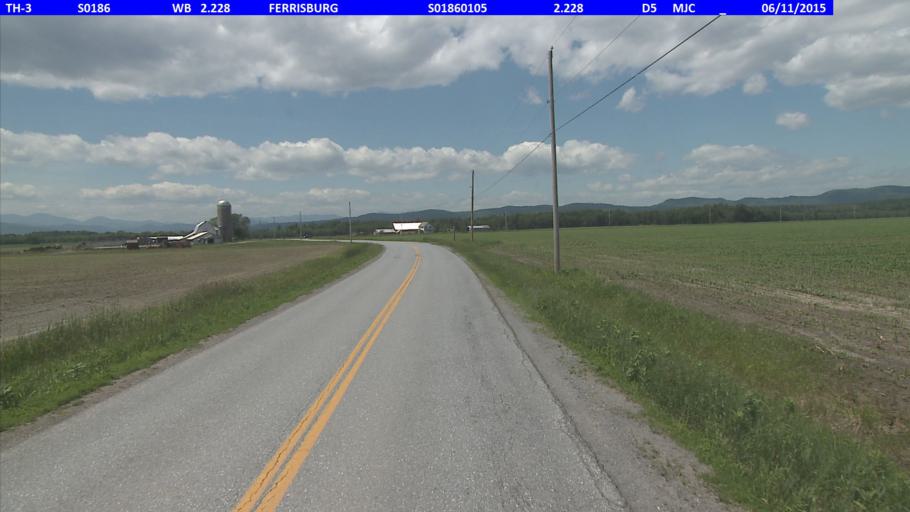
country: US
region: Vermont
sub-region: Addison County
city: Vergennes
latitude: 44.1911
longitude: -73.3207
